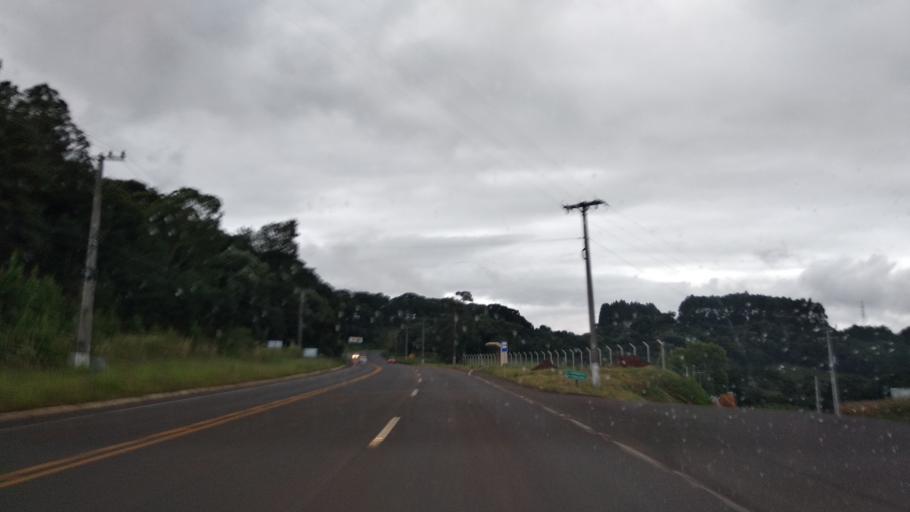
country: BR
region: Santa Catarina
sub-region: Videira
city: Videira
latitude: -27.0536
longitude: -51.1871
